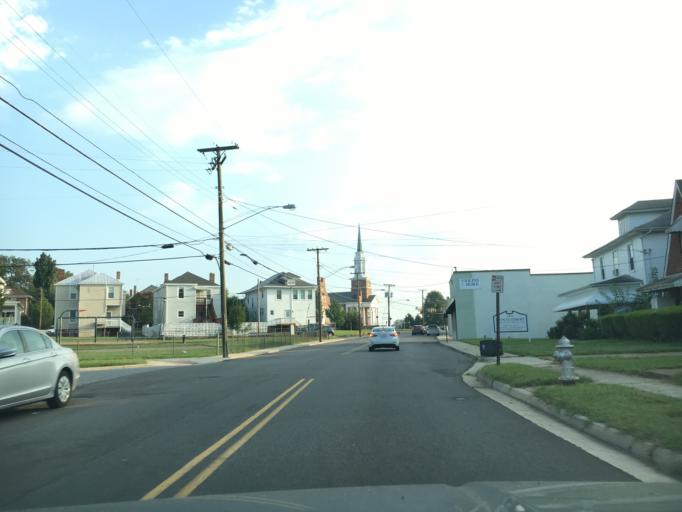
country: US
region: Virginia
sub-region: City of Lynchburg
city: West Lynchburg
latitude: 37.3953
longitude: -79.1716
